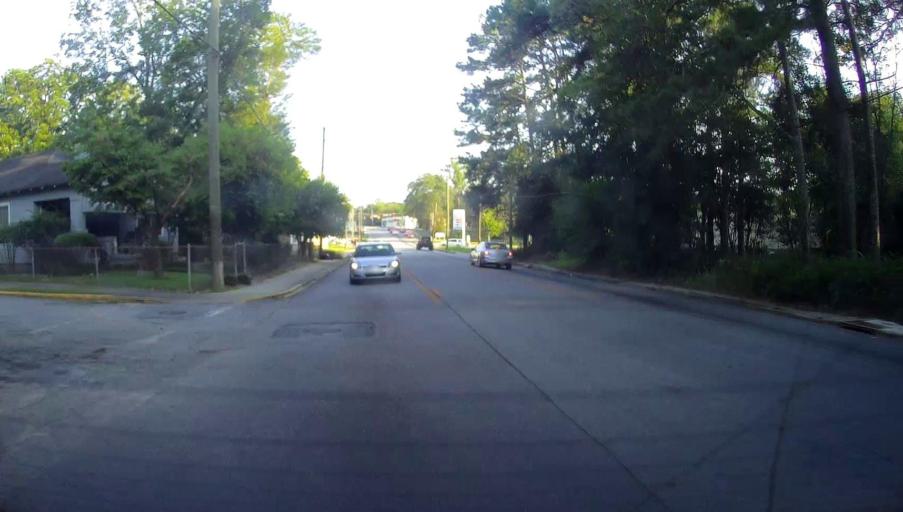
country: US
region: Georgia
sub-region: Bibb County
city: Macon
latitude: 32.8437
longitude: -83.6877
